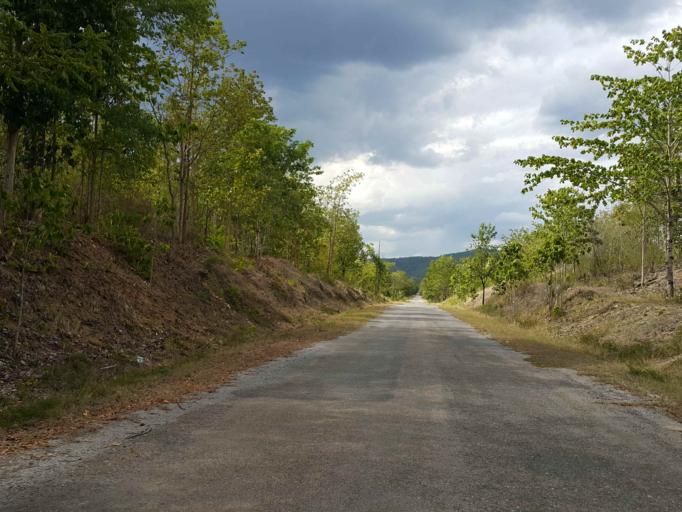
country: TH
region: Sukhothai
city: Thung Saliam
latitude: 17.3312
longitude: 99.4239
